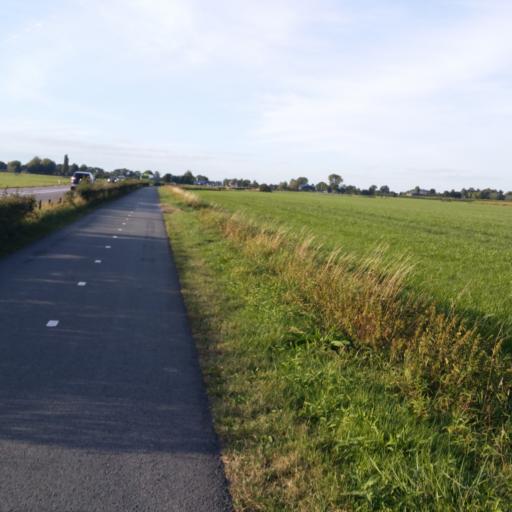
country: NL
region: Utrecht
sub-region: Gemeente Lopik
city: Lopik
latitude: 51.9971
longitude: 4.9668
